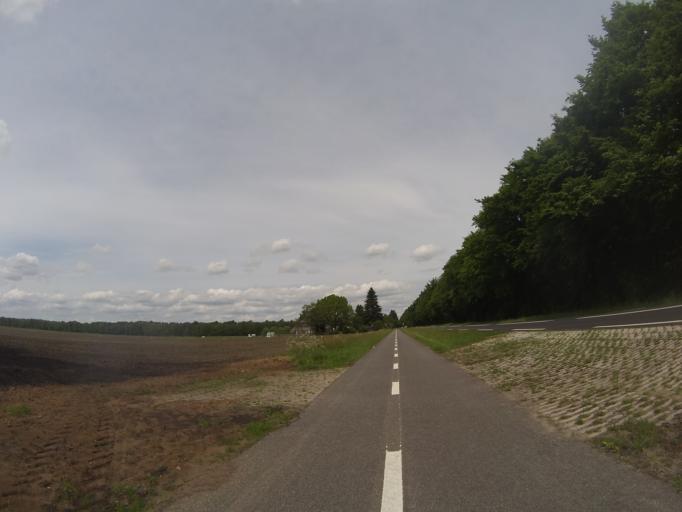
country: NL
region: Drenthe
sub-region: Gemeente Borger-Odoorn
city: Borger
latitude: 52.8773
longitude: 6.7220
